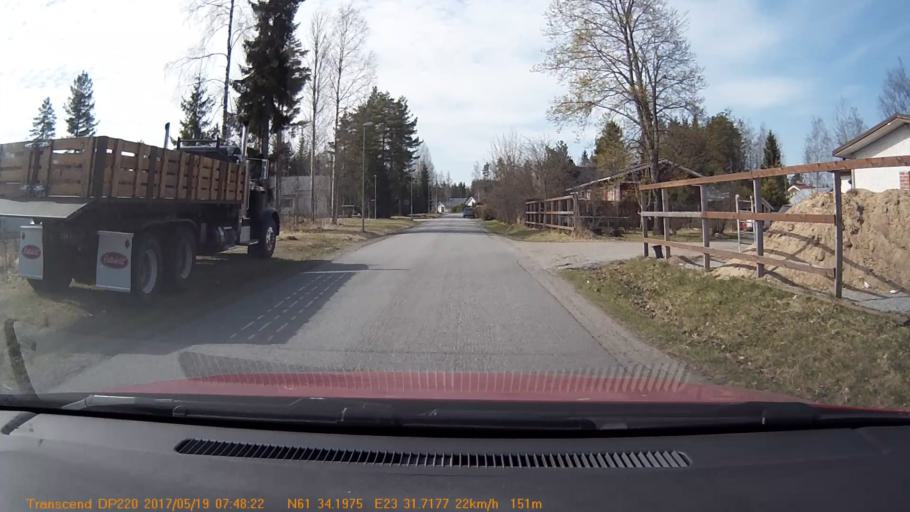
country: FI
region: Pirkanmaa
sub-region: Tampere
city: Yloejaervi
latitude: 61.5699
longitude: 23.5286
